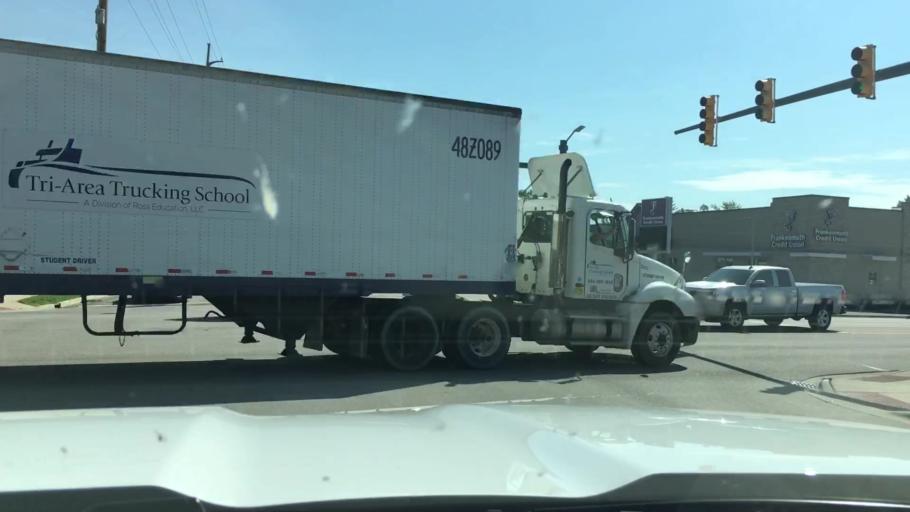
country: US
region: Michigan
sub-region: Saginaw County
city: Freeland
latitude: 43.5249
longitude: -84.1232
